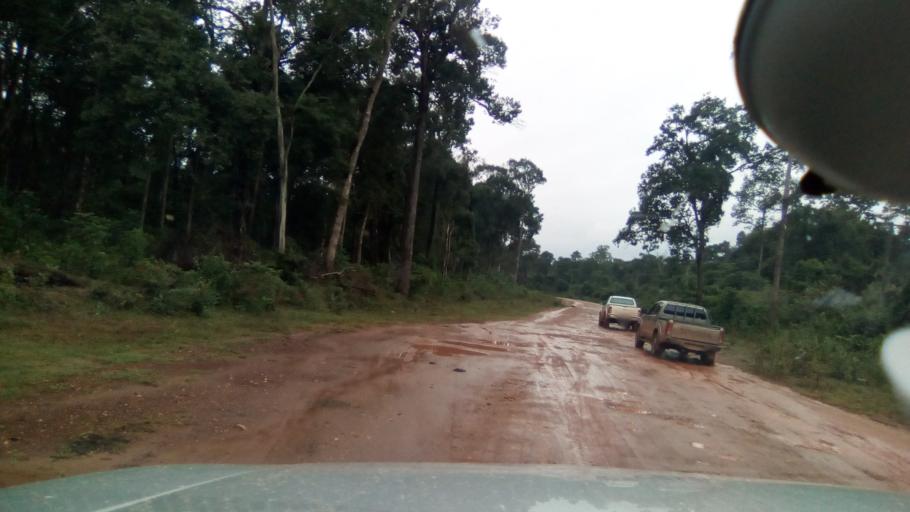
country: LA
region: Attapu
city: Attapu
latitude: 14.6781
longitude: 106.5592
